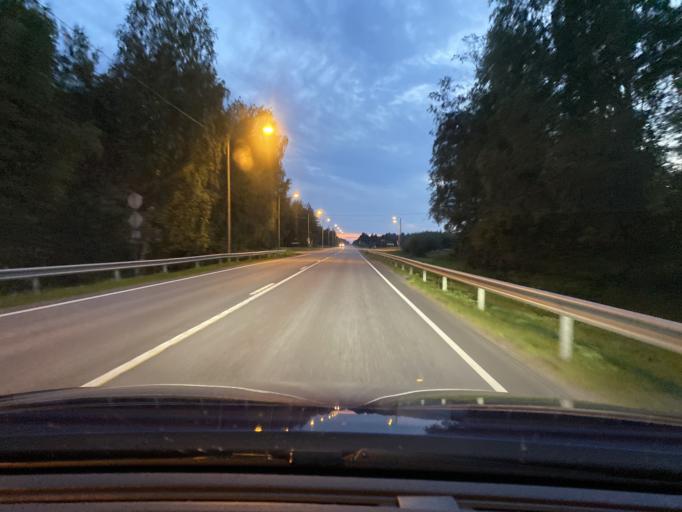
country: FI
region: Southern Ostrobothnia
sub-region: Suupohja
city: Kauhajoki
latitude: 62.4601
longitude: 22.1195
